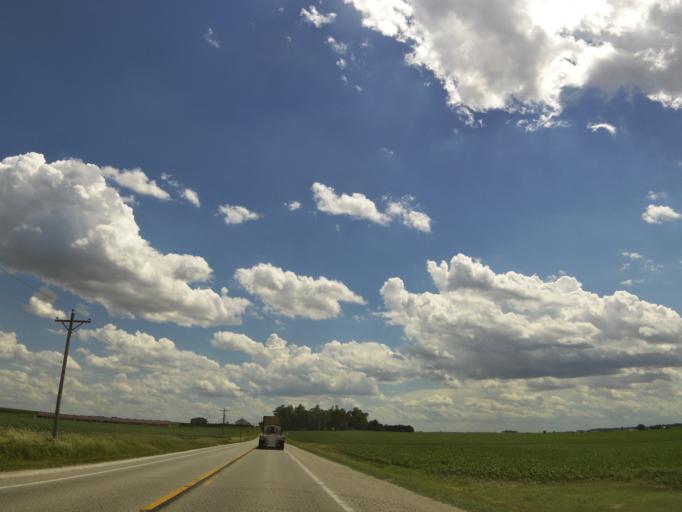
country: US
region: Iowa
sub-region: Benton County
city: Urbana
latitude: 42.3347
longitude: -91.8894
